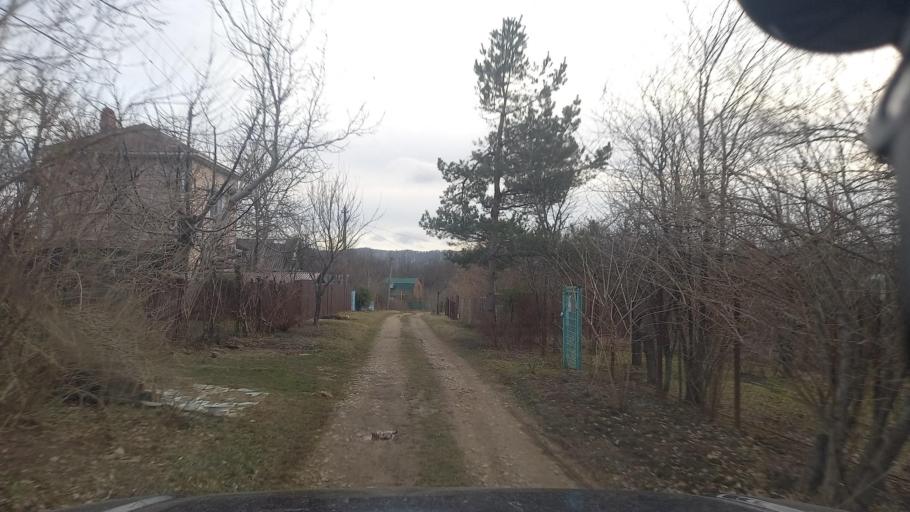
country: RU
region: Krasnodarskiy
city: Goryachiy Klyuch
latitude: 44.6917
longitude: 39.0157
